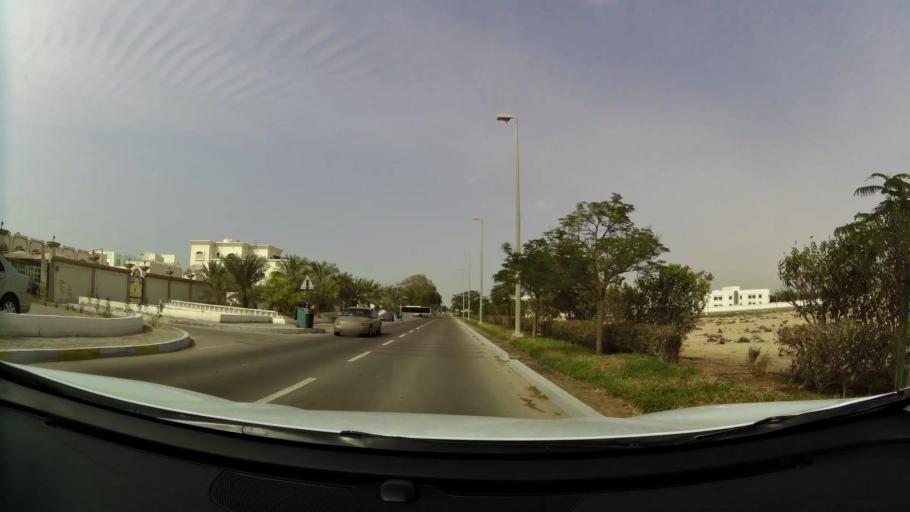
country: AE
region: Abu Dhabi
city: Abu Dhabi
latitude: 24.5682
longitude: 54.6929
